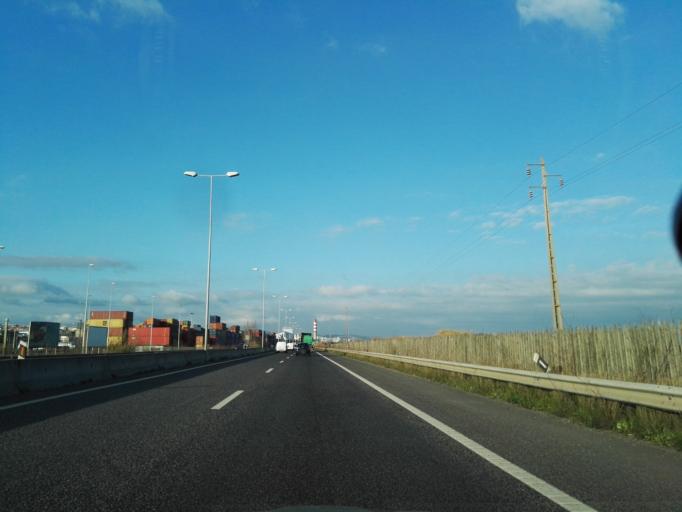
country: PT
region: Lisbon
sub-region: Loures
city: Sao Joao da Talha
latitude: 38.8151
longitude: -9.0878
